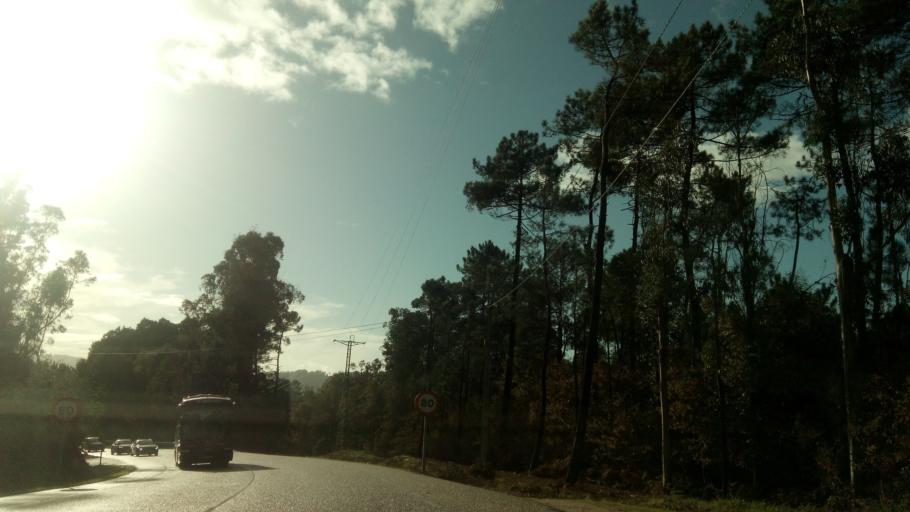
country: ES
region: Galicia
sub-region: Provincia de Pontevedra
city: Ponteareas
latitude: 42.2141
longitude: -8.5039
